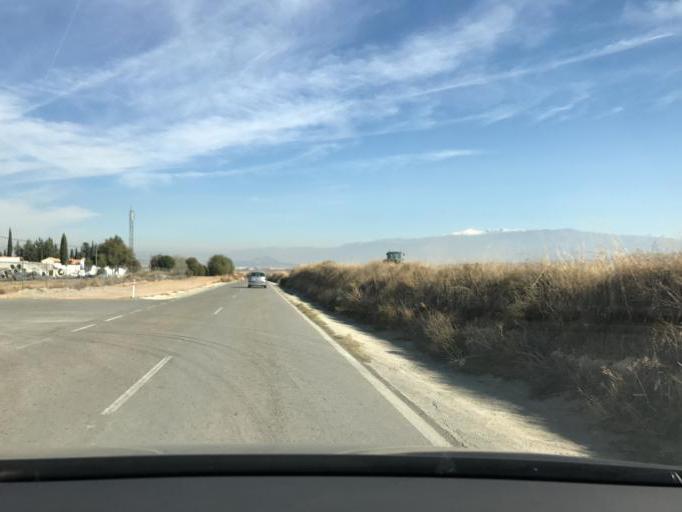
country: ES
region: Andalusia
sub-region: Provincia de Granada
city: Ventas de Huelma
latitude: 37.0710
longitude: -3.8121
